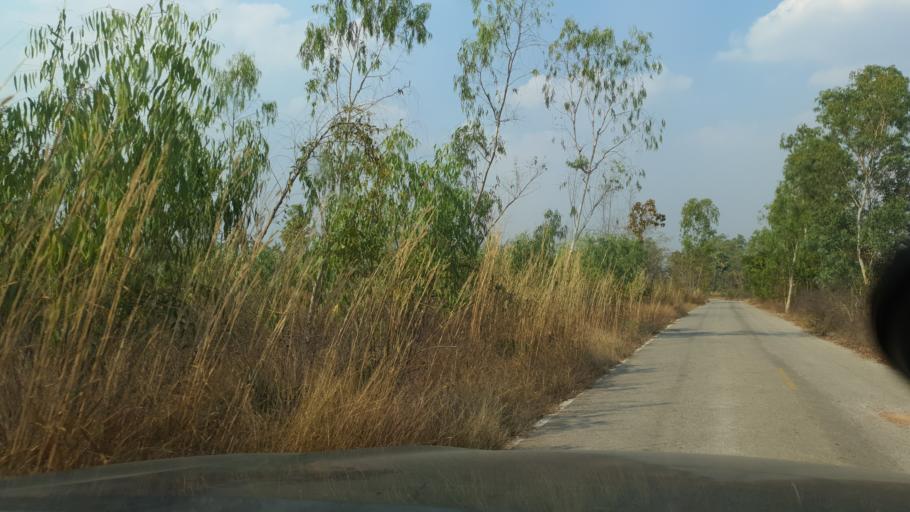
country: TH
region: Sukhothai
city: Ban Dan Lan Hoi
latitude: 17.0068
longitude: 99.5584
